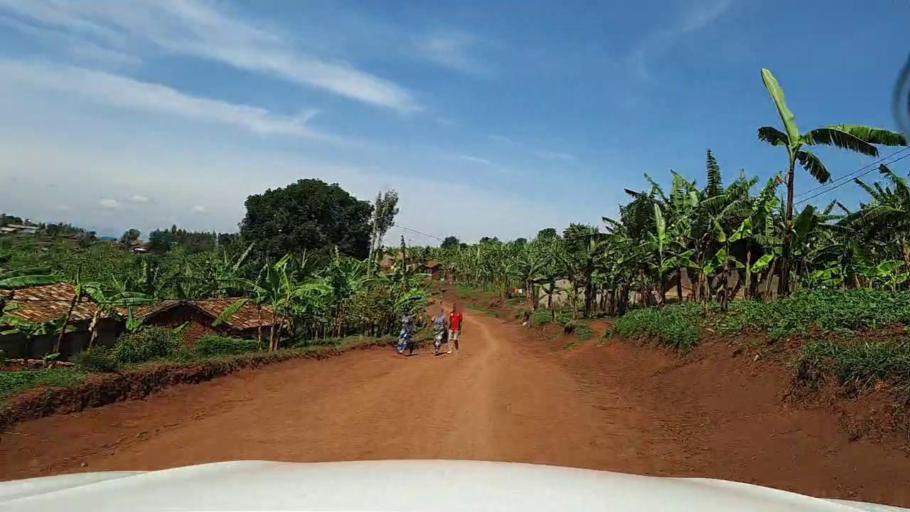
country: RW
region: Southern Province
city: Butare
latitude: -2.7055
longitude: 29.8436
